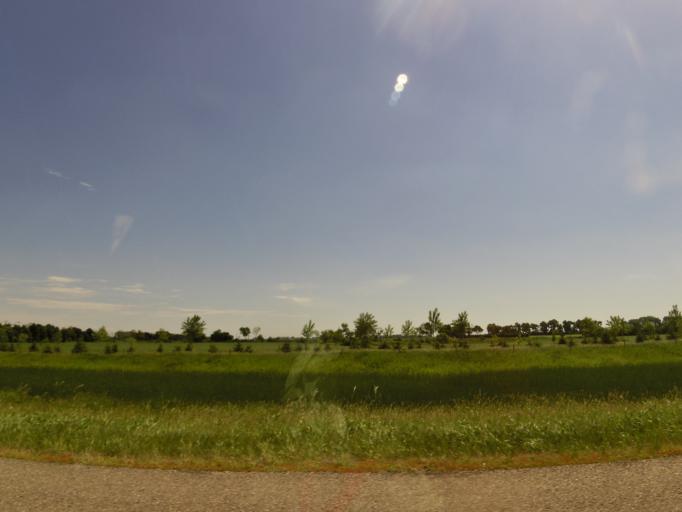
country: US
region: North Dakota
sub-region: Grand Forks County
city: Grand Forks
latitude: 47.7821
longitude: -97.0776
